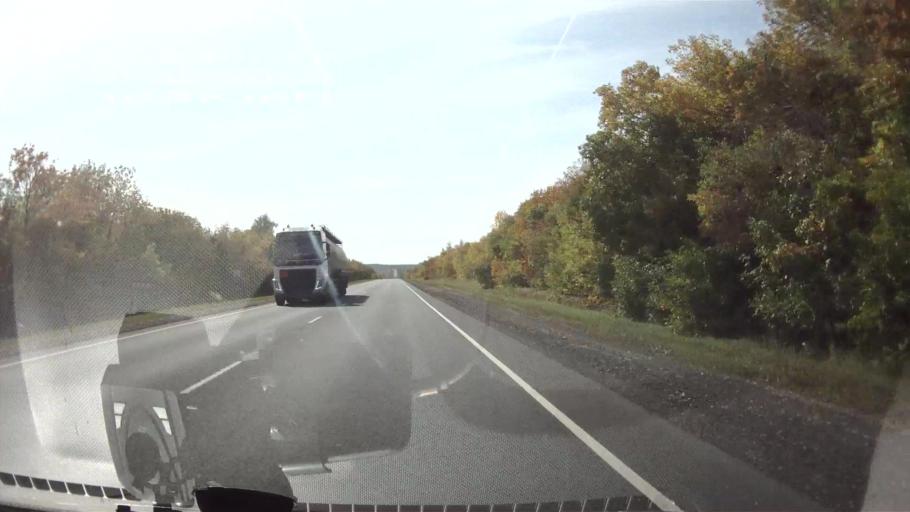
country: RU
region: Saratov
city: Khvalynsk
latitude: 52.5970
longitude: 48.1390
